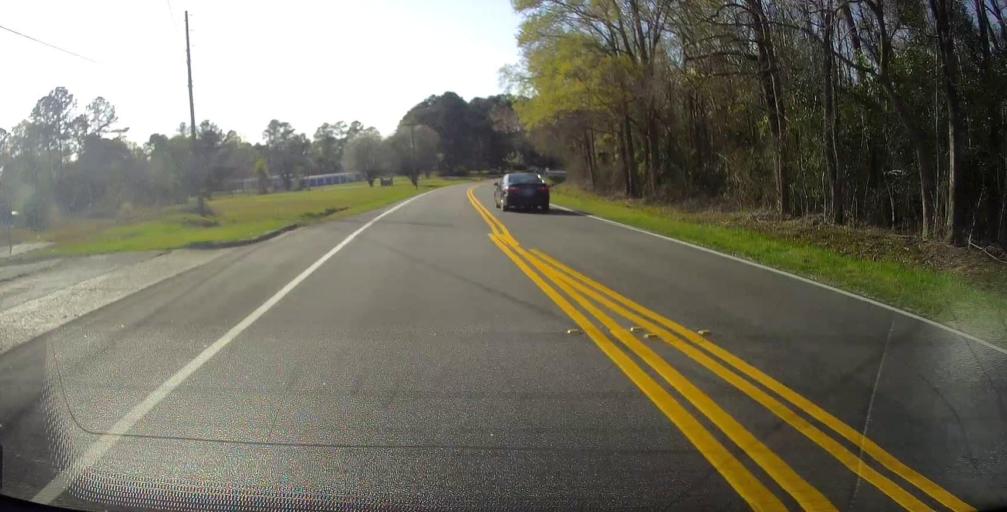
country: US
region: Georgia
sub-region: Montgomery County
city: Mount Vernon
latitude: 32.1785
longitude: -82.5986
